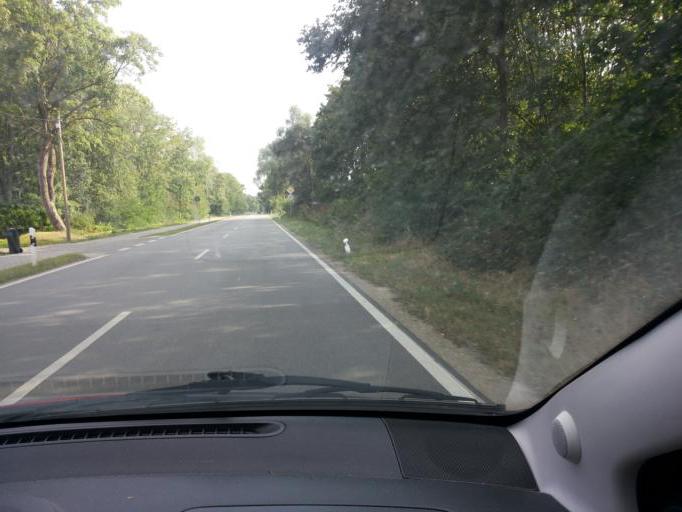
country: DE
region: Bavaria
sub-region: Upper Bavaria
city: Gaimersheim
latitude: 48.7749
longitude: 11.3571
